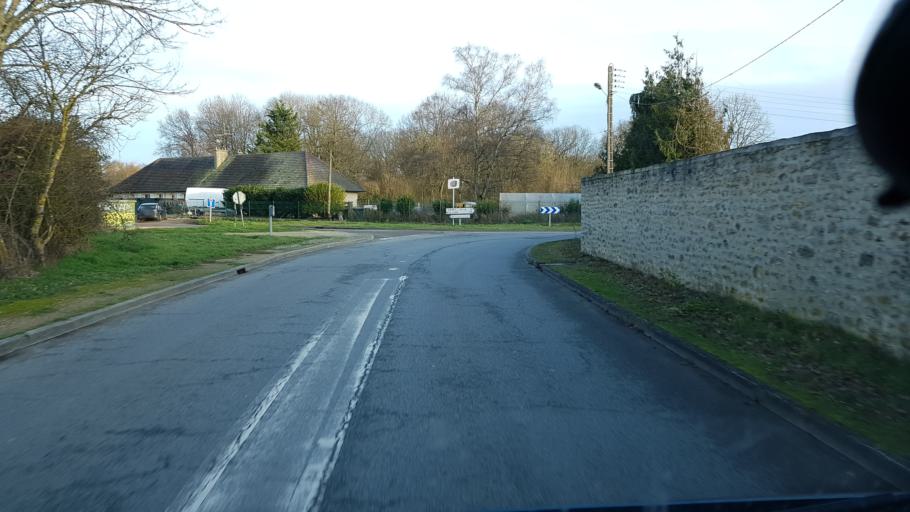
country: FR
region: Ile-de-France
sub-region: Departement des Yvelines
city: Auffargis
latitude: 48.6762
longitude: 1.9161
